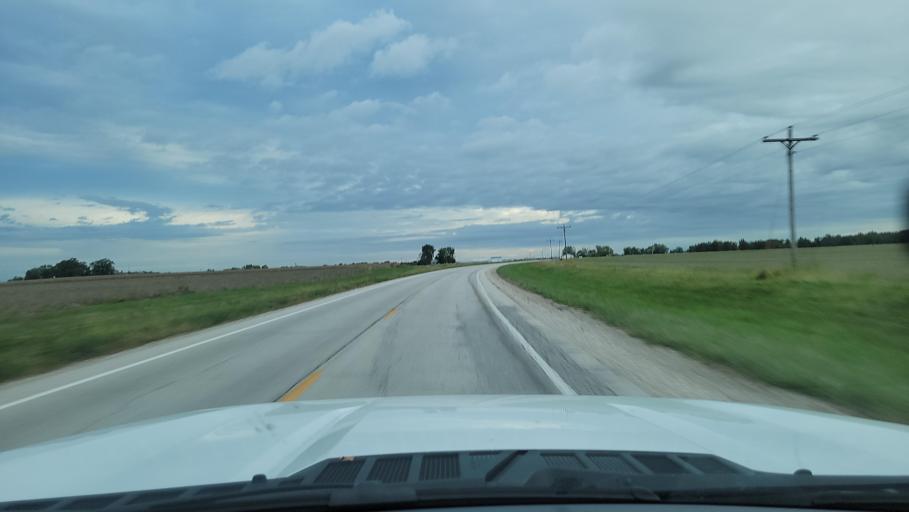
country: US
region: Illinois
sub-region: Schuyler County
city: Rushville
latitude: 40.0754
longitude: -90.6151
